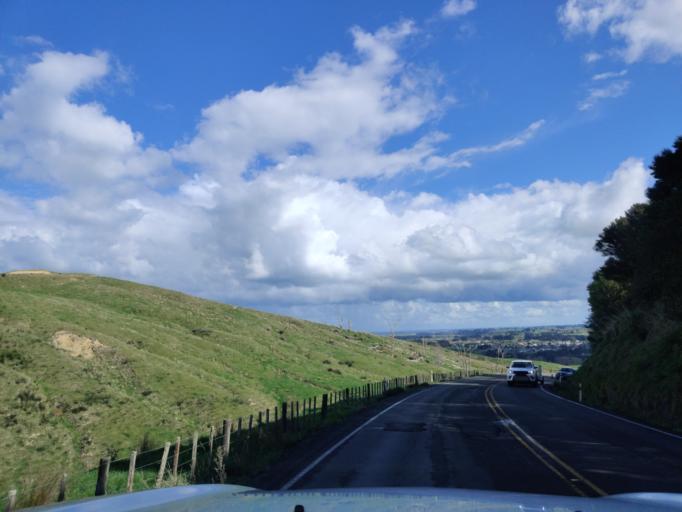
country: NZ
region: Manawatu-Wanganui
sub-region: Palmerston North City
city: Palmerston North
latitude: -40.2856
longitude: 175.7794
